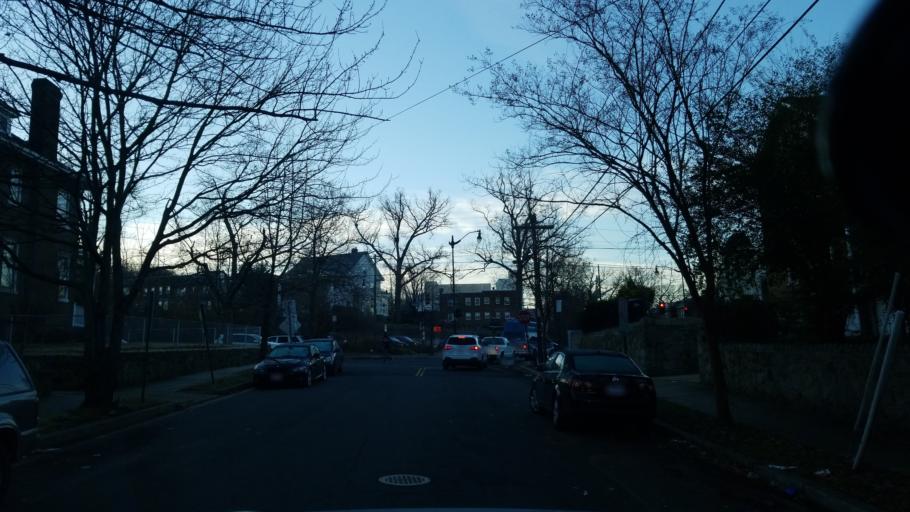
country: US
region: Maryland
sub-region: Prince George's County
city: Silver Hill
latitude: 38.8725
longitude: -76.9664
